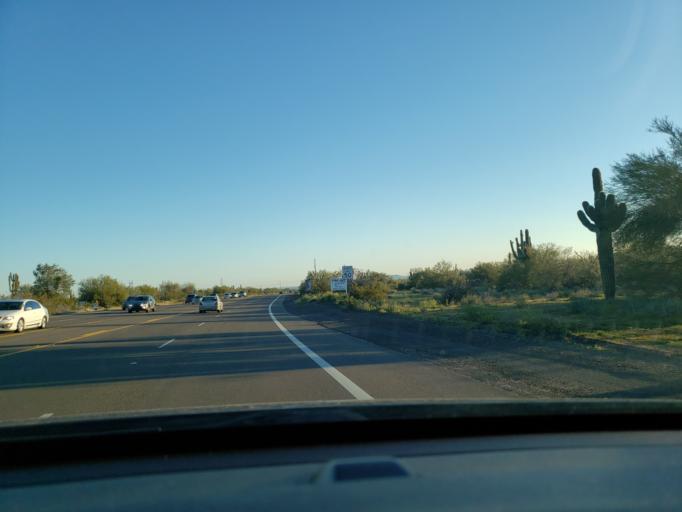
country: US
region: Arizona
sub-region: Maricopa County
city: Carefree
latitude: 33.7257
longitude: -111.9255
